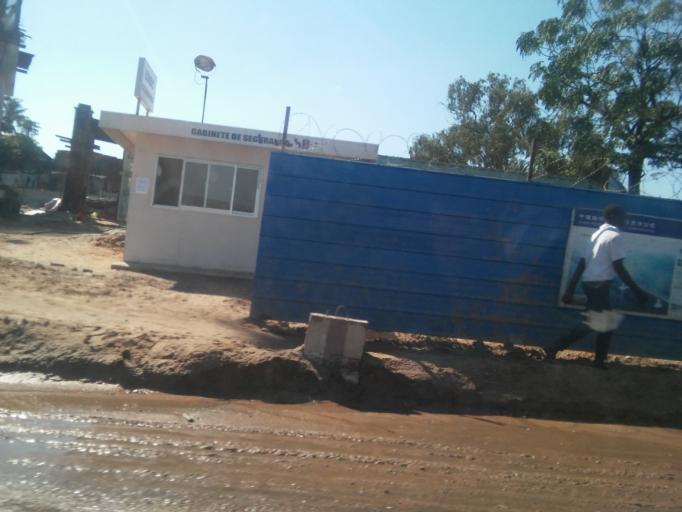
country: MZ
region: Maputo City
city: Maputo
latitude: -25.9543
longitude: 32.5543
